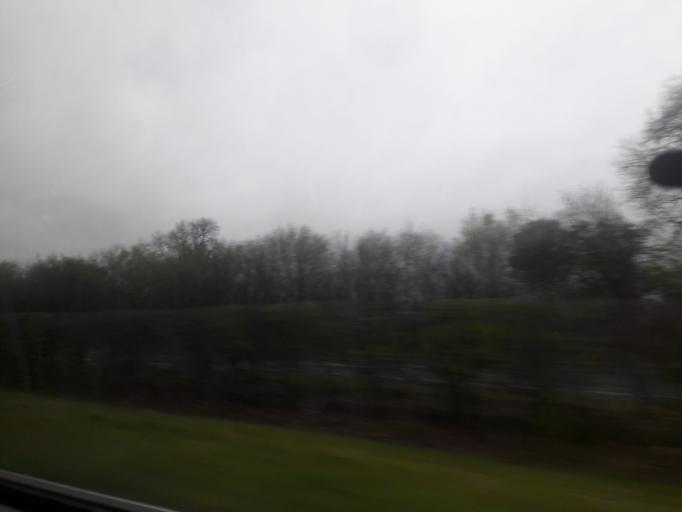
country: IE
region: Leinster
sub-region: An Iarmhi
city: An Muileann gCearr
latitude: 53.5302
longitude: -7.3083
